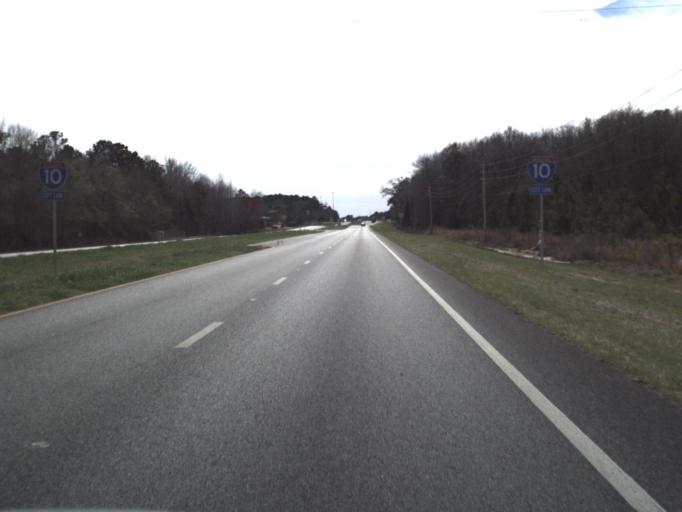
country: US
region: Florida
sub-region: Jackson County
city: Marianna
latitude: 30.7654
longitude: -85.3762
